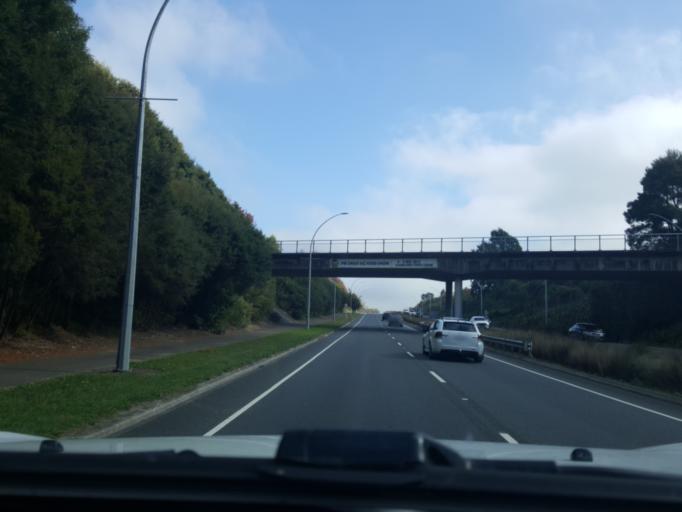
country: NZ
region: Waikato
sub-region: Hamilton City
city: Hamilton
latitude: -37.7454
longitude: 175.2489
